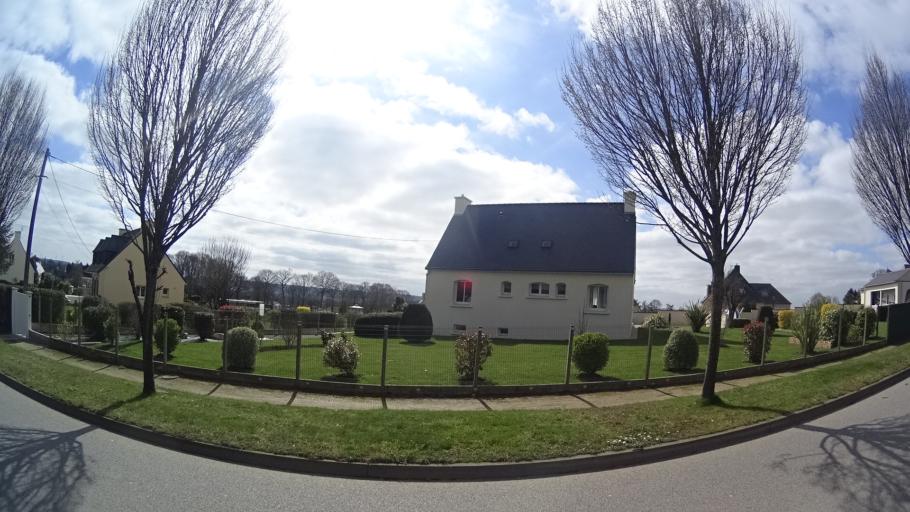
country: FR
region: Brittany
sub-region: Departement du Morbihan
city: Ruffiac
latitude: 47.8219
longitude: -2.2857
